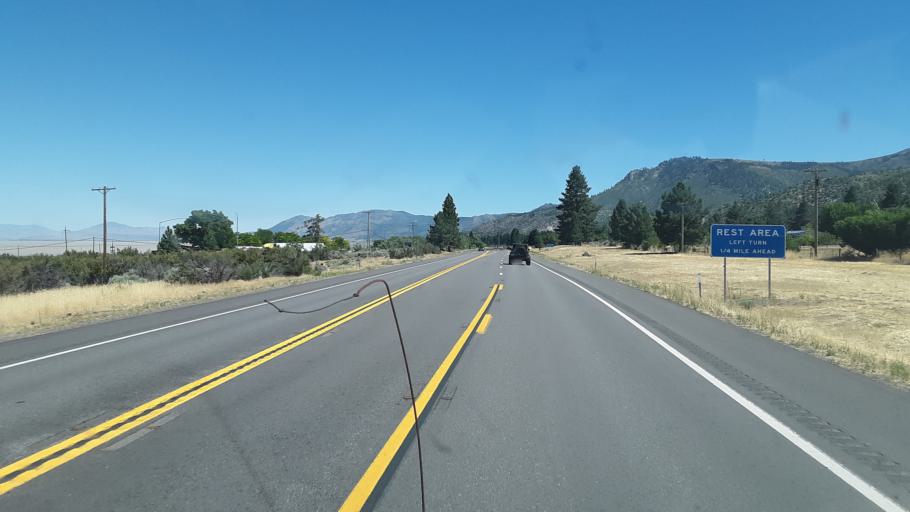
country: US
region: California
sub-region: Lassen County
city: Janesville
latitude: 40.2585
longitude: -120.4680
